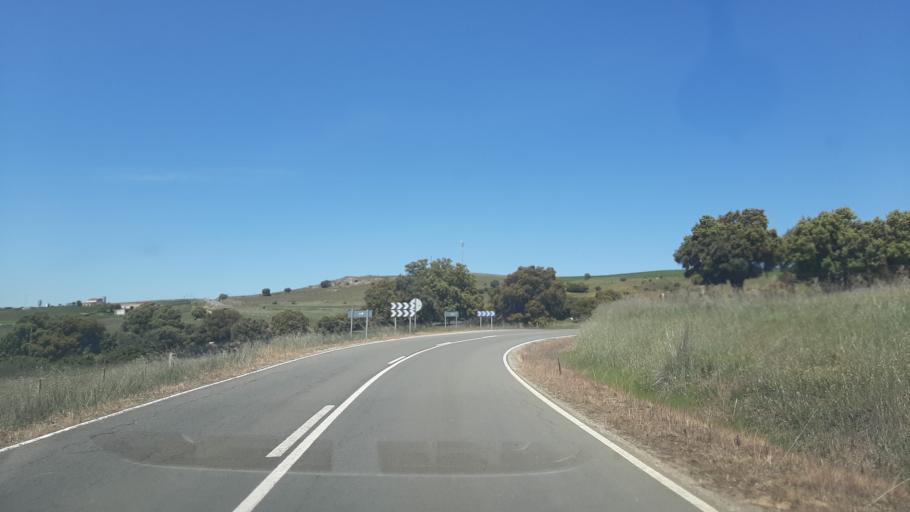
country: ES
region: Castille and Leon
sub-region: Provincia de Salamanca
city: Puente del Congosto
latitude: 40.5346
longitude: -5.5650
